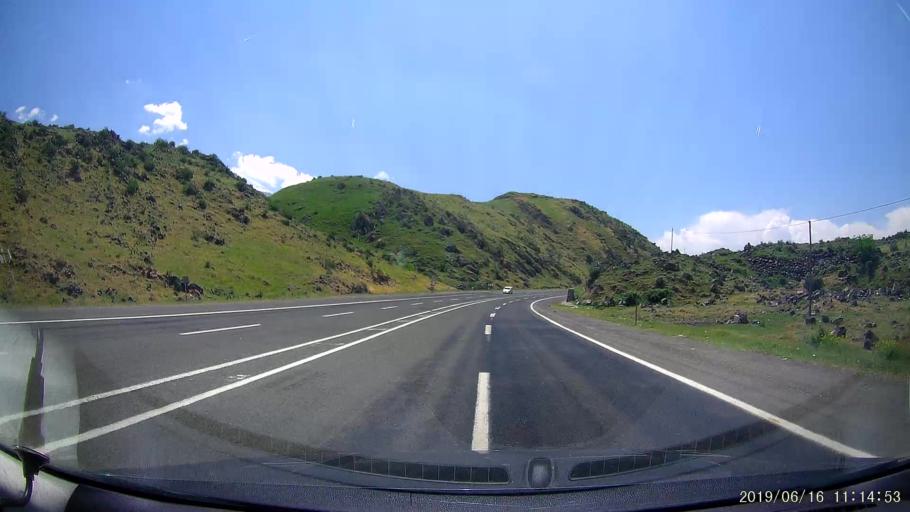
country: TR
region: Igdir
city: Igdir
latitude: 39.7721
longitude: 44.1429
